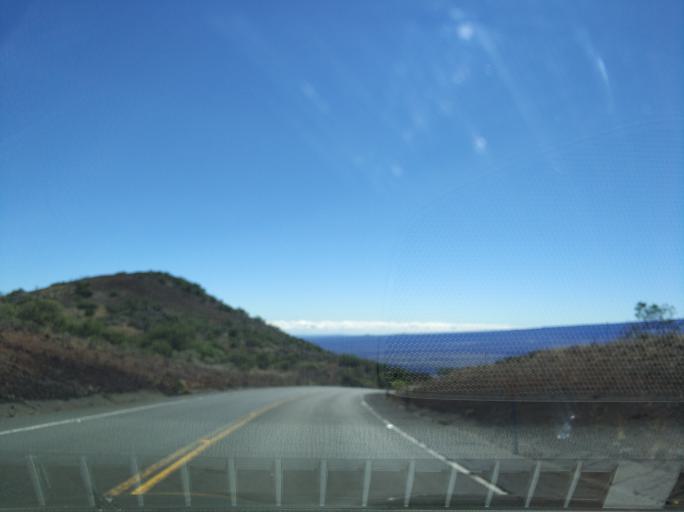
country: US
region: Hawaii
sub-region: Hawaii County
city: Honoka'a
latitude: 19.7519
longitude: -155.4558
